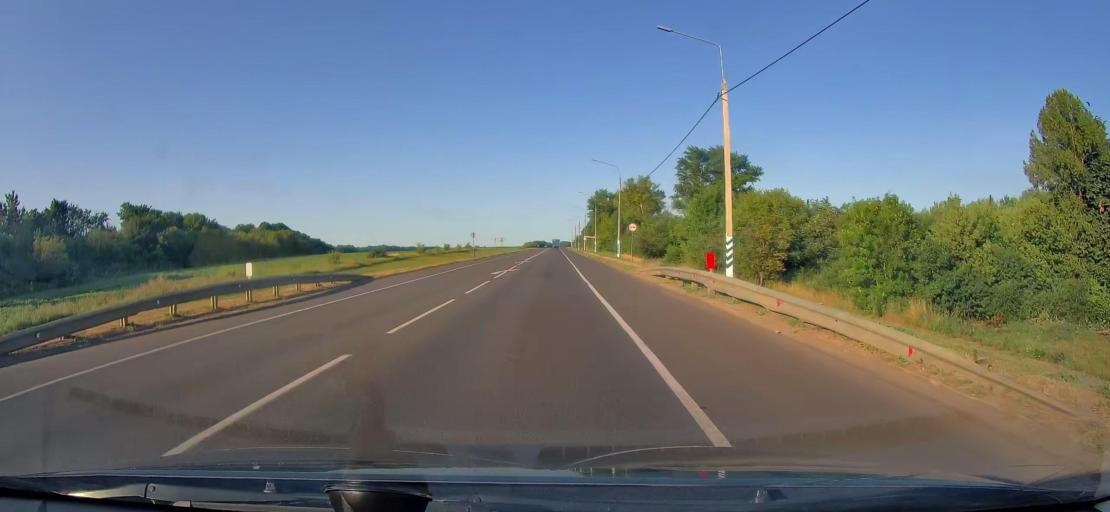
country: RU
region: Tula
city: Plavsk
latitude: 53.6480
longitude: 37.2232
